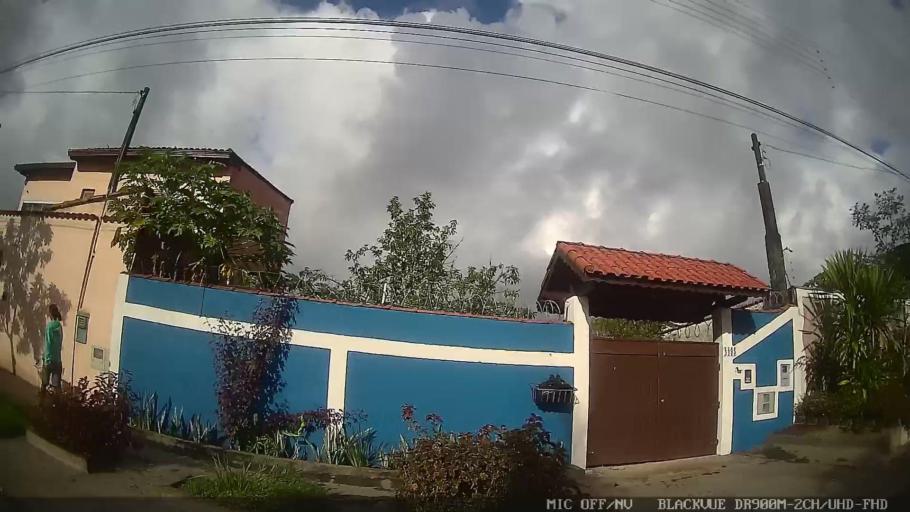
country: BR
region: Sao Paulo
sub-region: Itanhaem
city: Itanhaem
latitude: -24.1925
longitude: -46.8641
